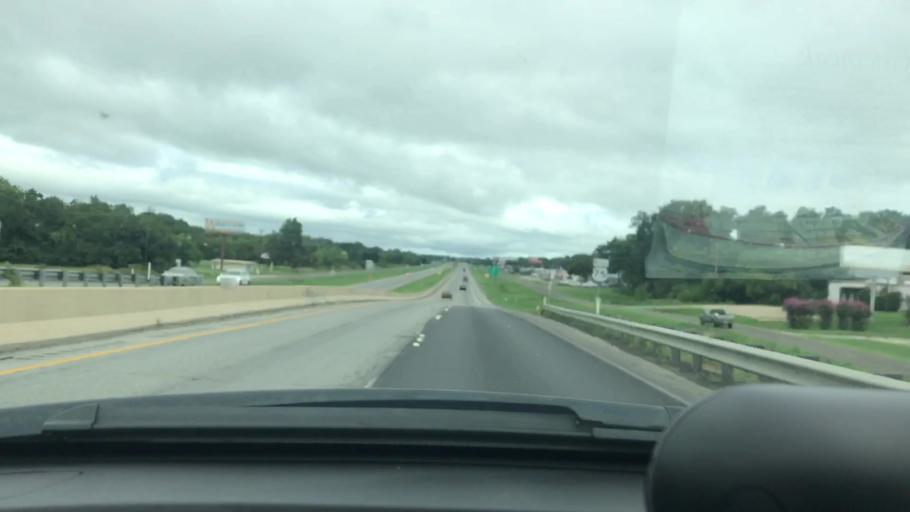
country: US
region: Texas
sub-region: Grayson County
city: Sherman
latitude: 33.6159
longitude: -96.6096
